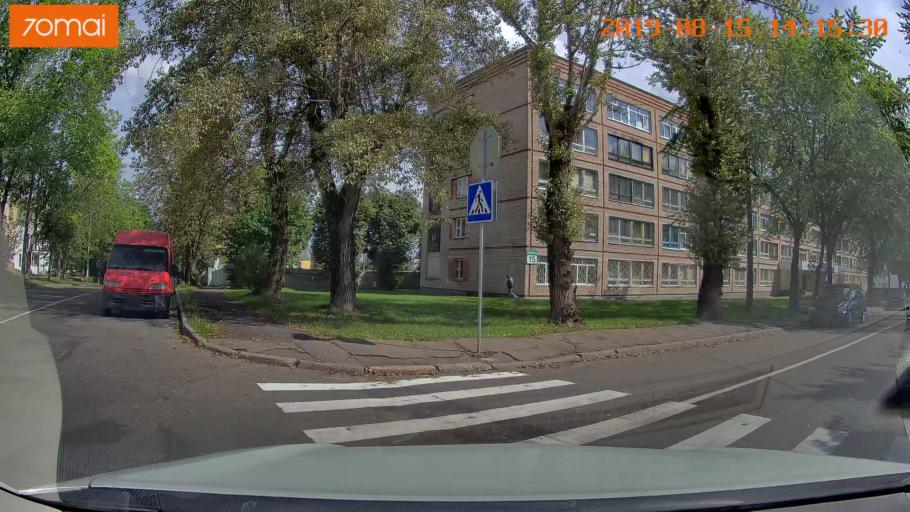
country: BY
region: Minsk
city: Minsk
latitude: 53.8886
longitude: 27.5912
